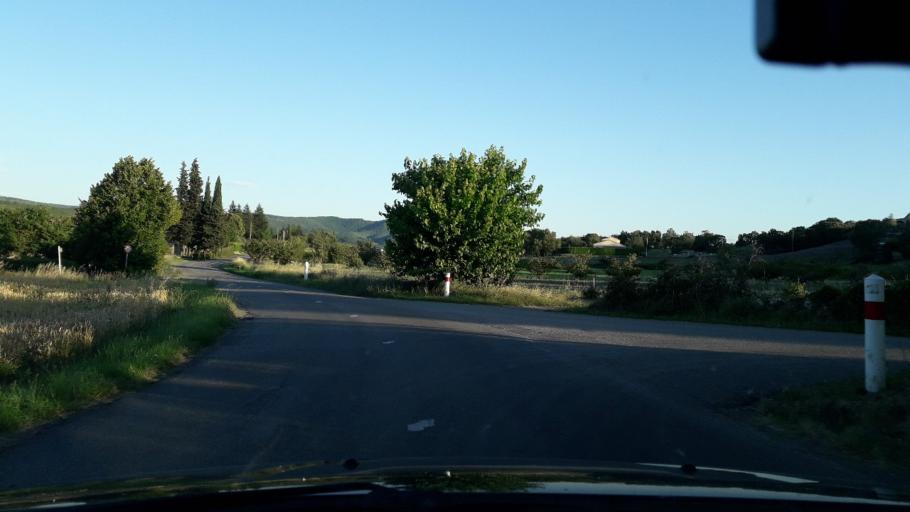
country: FR
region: Rhone-Alpes
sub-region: Departement de l'Ardeche
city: Lavilledieu
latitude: 44.5915
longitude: 4.4594
